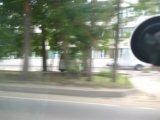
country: RU
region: Moskovskaya
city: Zhukovskiy
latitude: 55.6038
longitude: 38.1302
